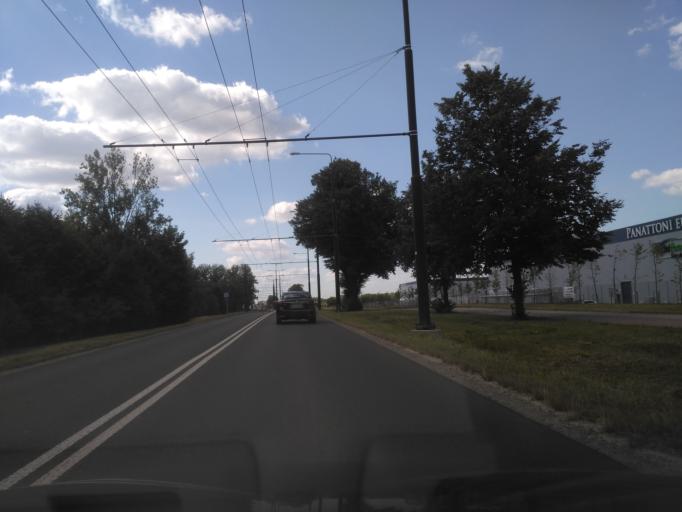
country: PL
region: Lublin Voivodeship
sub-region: Powiat lubelski
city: Jakubowice Murowane
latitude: 51.2199
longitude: 22.6228
